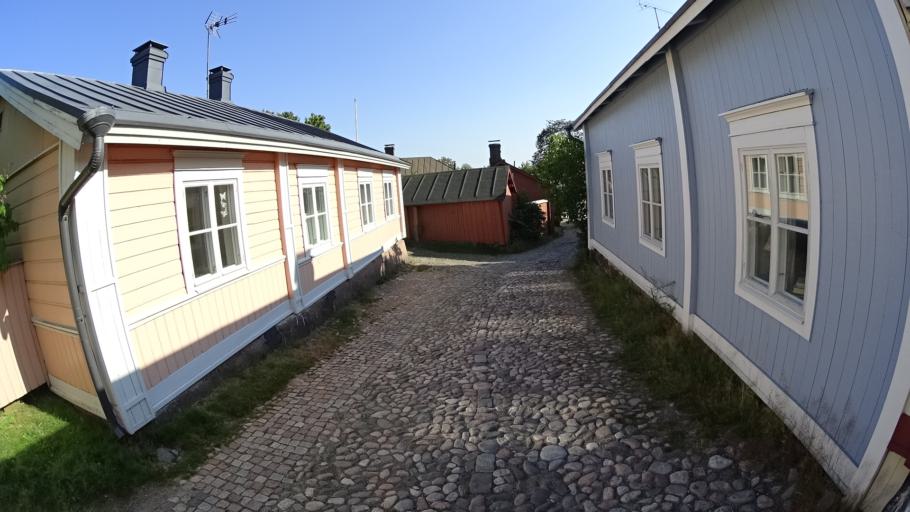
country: FI
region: Uusimaa
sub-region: Porvoo
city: Porvoo
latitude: 60.3973
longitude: 25.6616
